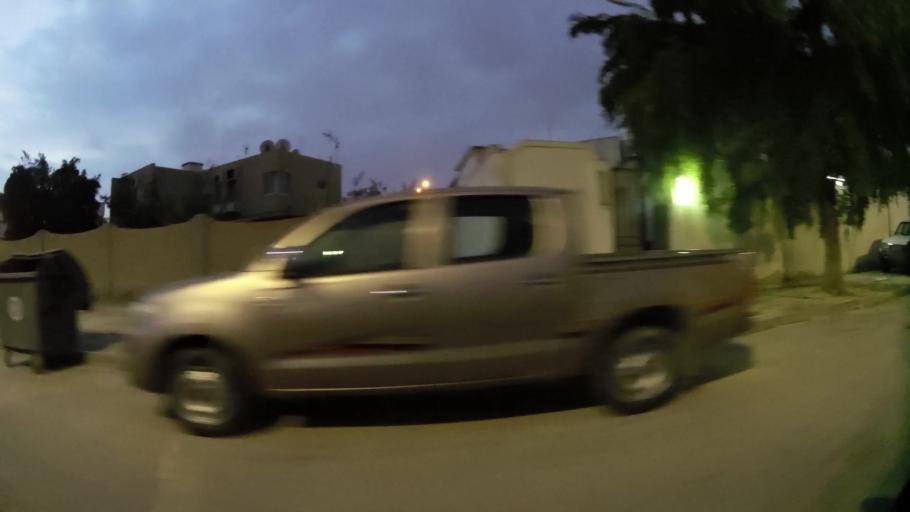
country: QA
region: Baladiyat ad Dawhah
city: Doha
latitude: 25.3434
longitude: 51.5066
